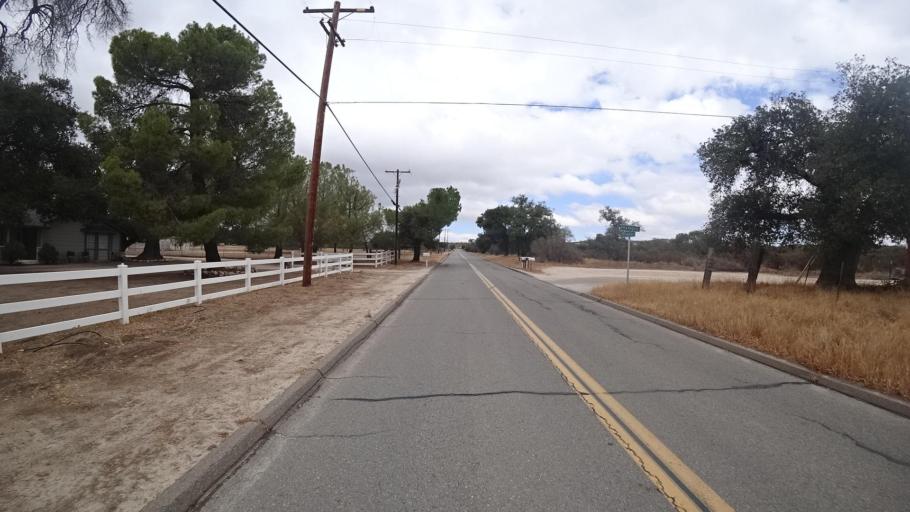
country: MX
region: Baja California
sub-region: Tecate
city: Cereso del Hongo
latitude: 32.6150
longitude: -116.3204
